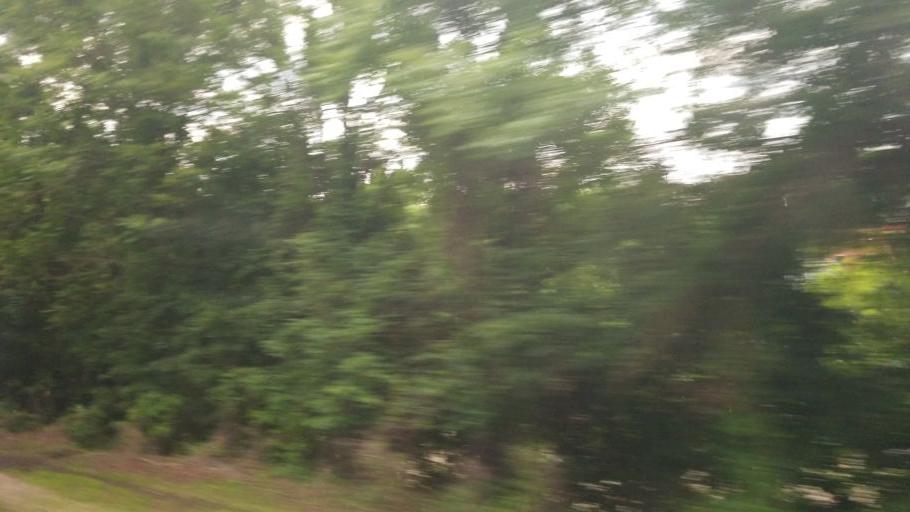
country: US
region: Pennsylvania
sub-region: Allegheny County
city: Bloomfield
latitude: 40.4395
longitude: -79.9499
